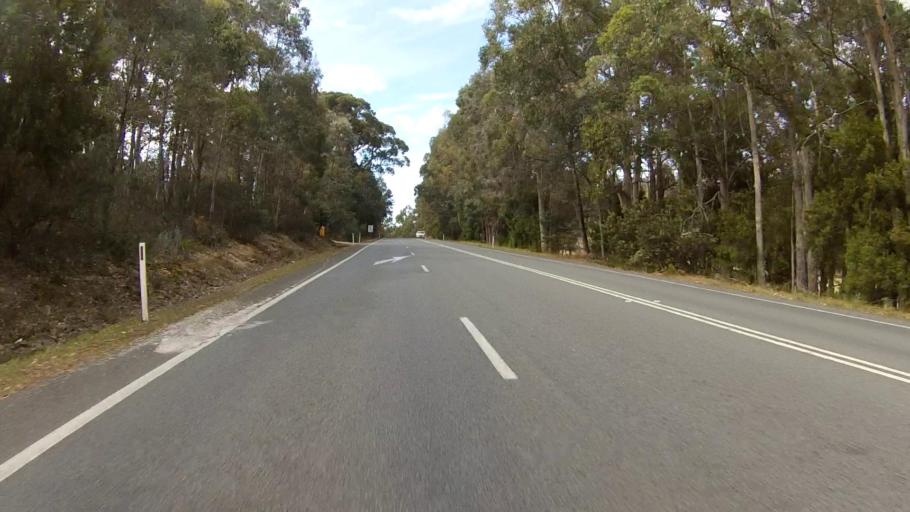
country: AU
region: Tasmania
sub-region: Kingborough
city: Kettering
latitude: -43.1100
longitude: 147.2423
